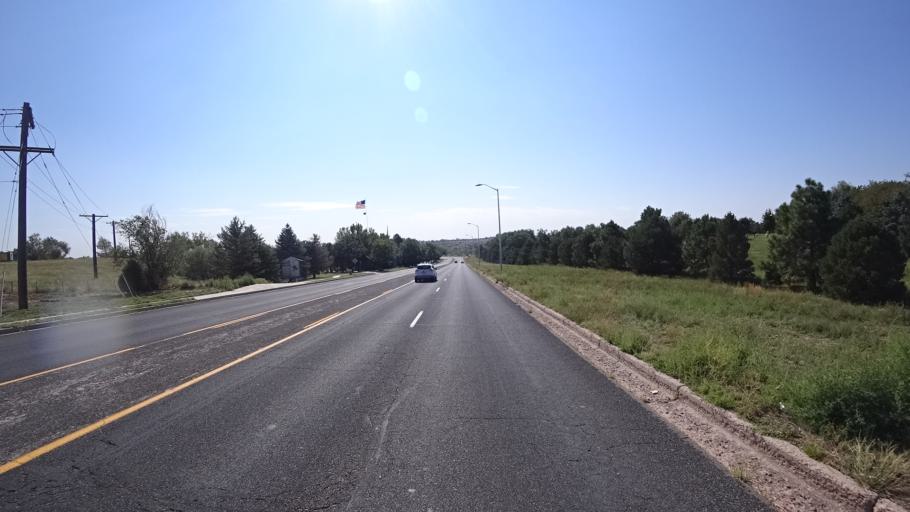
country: US
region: Colorado
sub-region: El Paso County
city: Colorado Springs
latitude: 38.8197
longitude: -104.7964
